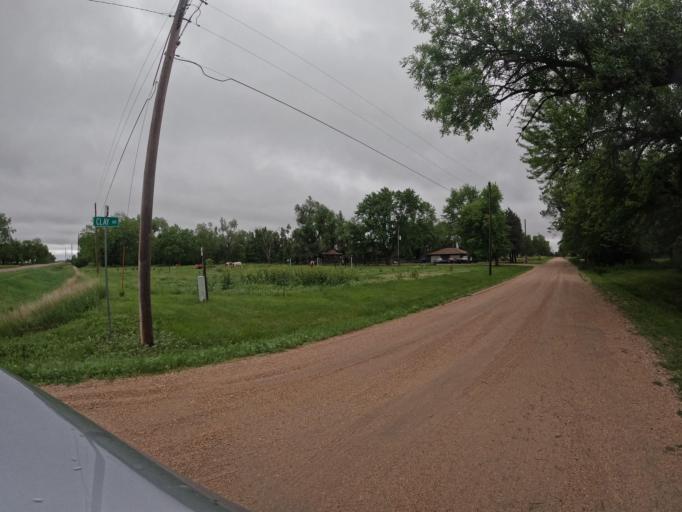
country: US
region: Nebraska
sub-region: Clay County
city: Harvard
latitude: 40.6261
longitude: -98.0968
